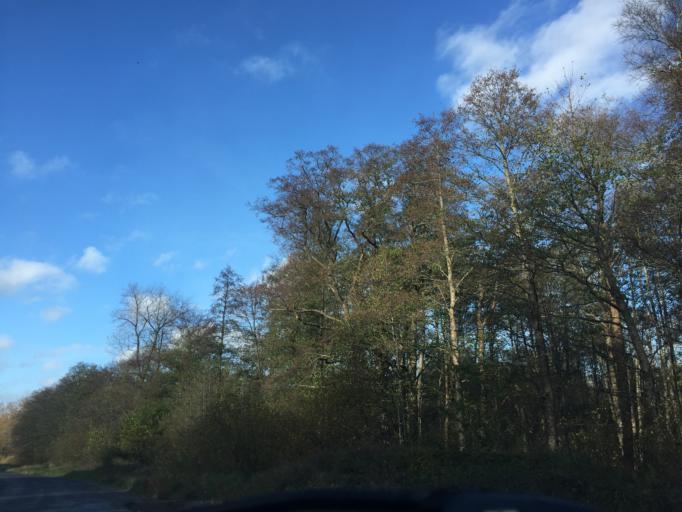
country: LV
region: Liepaja
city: Vec-Liepaja
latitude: 56.5839
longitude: 21.0337
